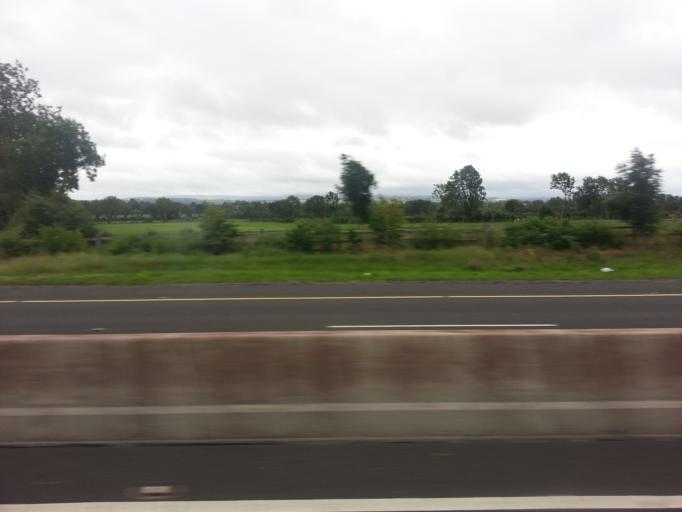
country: IE
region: Leinster
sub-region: County Carlow
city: Bagenalstown
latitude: 52.7010
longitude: -7.0205
